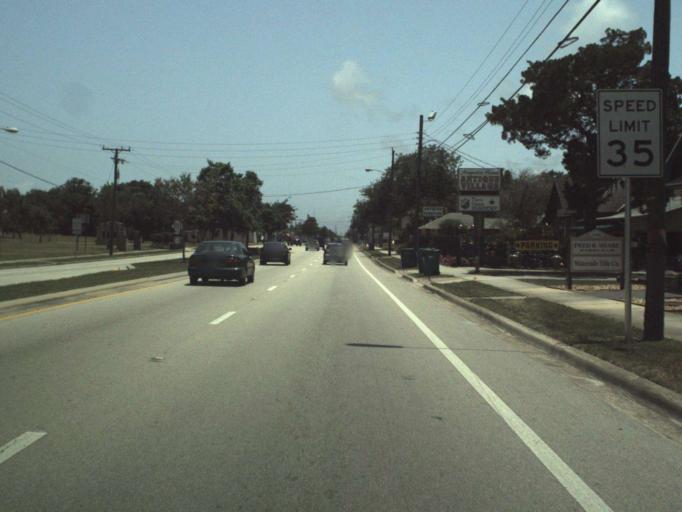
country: US
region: Florida
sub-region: Volusia County
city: Holly Hill
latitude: 29.2456
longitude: -81.0417
